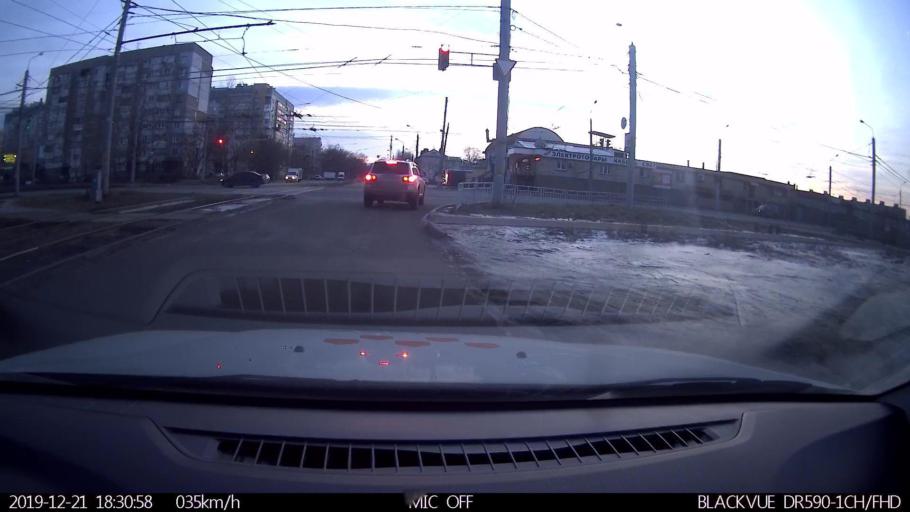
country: RU
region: Nizjnij Novgorod
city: Nizhniy Novgorod
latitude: 56.3351
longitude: 43.9190
